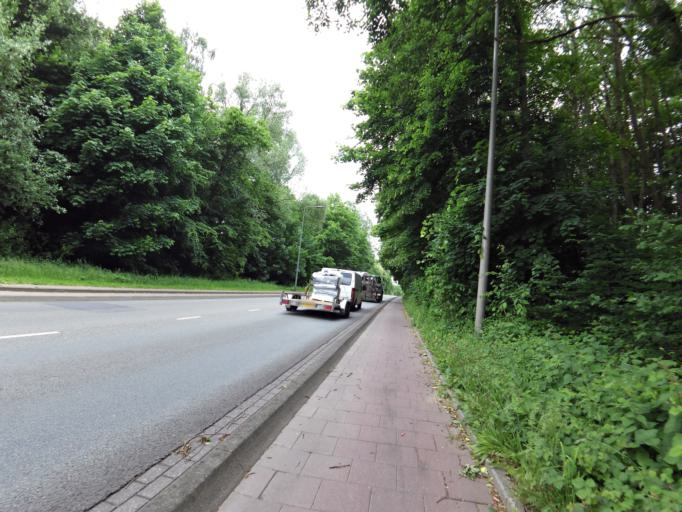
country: NL
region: Limburg
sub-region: Gemeente Kerkrade
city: Kerkrade
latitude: 50.8716
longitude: 6.0269
